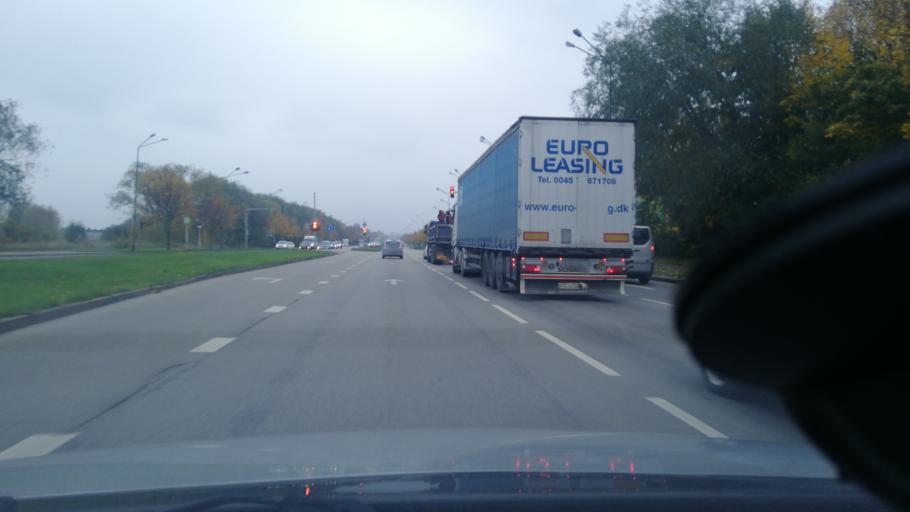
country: LT
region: Klaipedos apskritis
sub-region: Klaipeda
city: Klaipeda
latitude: 55.6759
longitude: 21.1921
